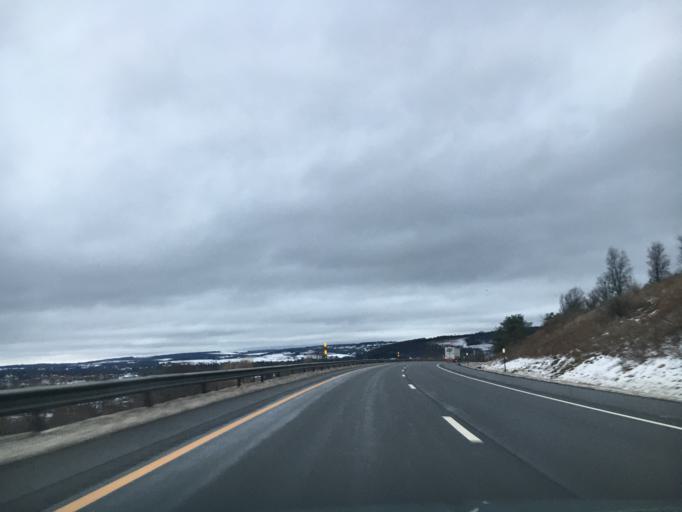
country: US
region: New York
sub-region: Cortland County
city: Cortland
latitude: 42.5989
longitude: -76.1525
